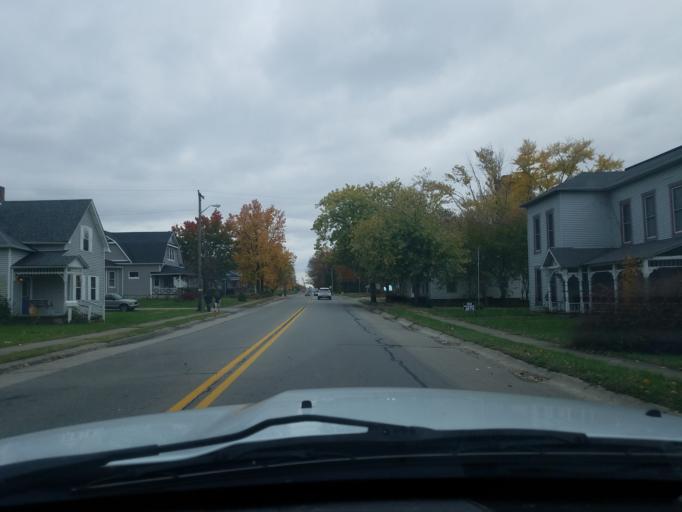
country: US
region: Indiana
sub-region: Bartholomew County
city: Hope
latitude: 39.3010
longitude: -85.7716
